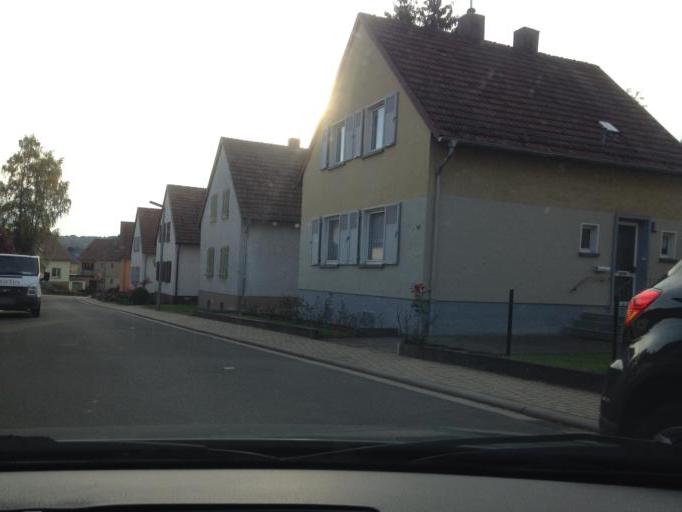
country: DE
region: Saarland
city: Ottweiler
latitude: 49.4101
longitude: 7.1564
